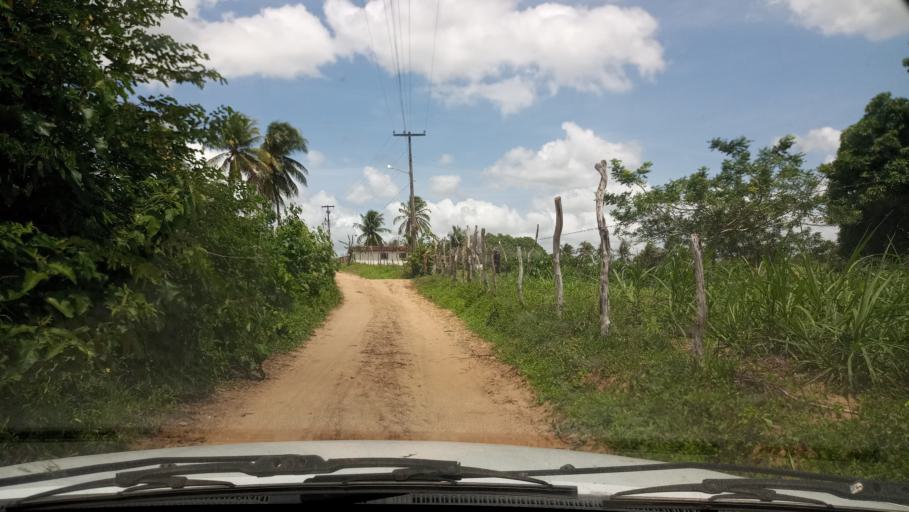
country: BR
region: Rio Grande do Norte
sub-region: Brejinho
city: Brejinho
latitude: -6.2623
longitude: -35.3737
